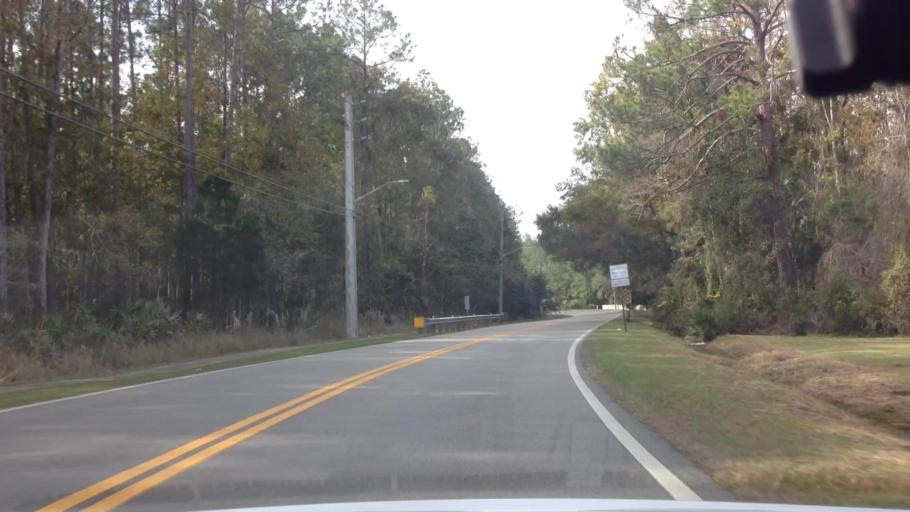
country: US
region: Florida
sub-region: Nassau County
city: Yulee
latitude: 30.5007
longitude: -81.5852
